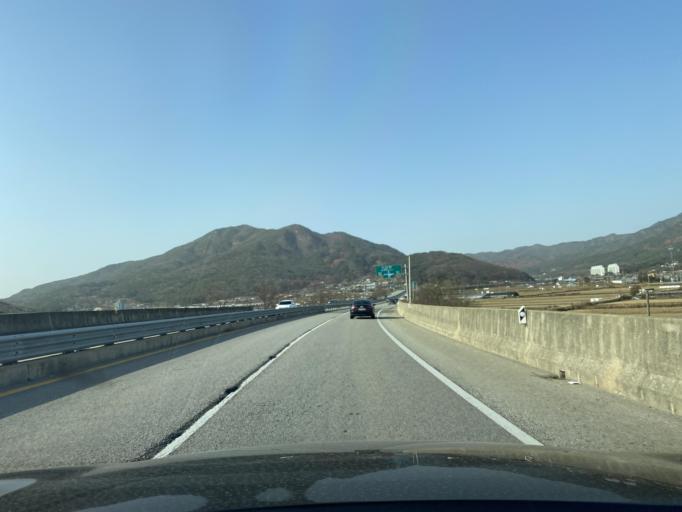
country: KR
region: Chungcheongnam-do
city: Hongsung
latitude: 36.6818
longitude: 126.6555
